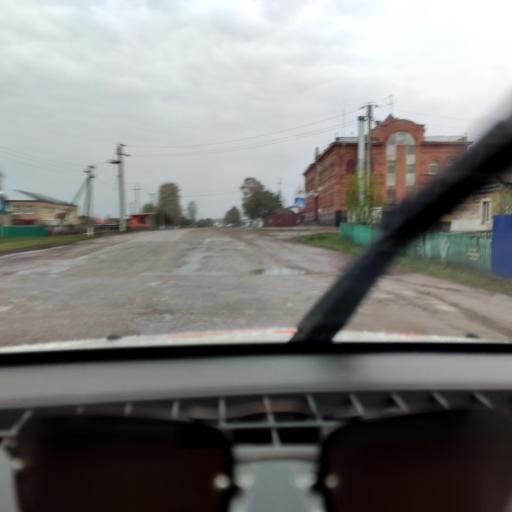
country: RU
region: Bashkortostan
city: Ulukulevo
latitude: 54.4320
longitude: 56.3232
